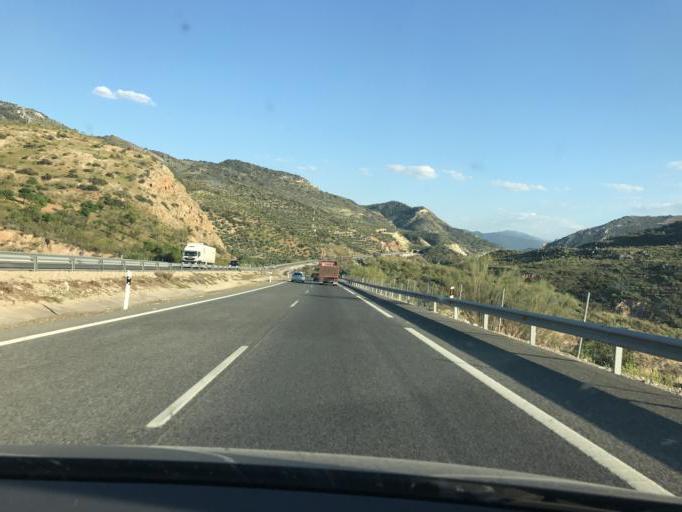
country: ES
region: Andalusia
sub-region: Provincia de Jaen
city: Pegalajar
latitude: 37.7142
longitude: -3.6456
